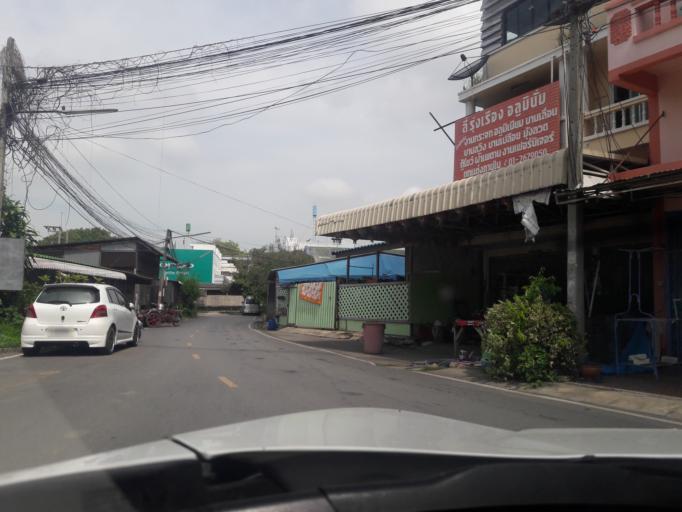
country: TH
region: Lop Buri
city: Ban Mi
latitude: 15.0406
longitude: 100.5420
